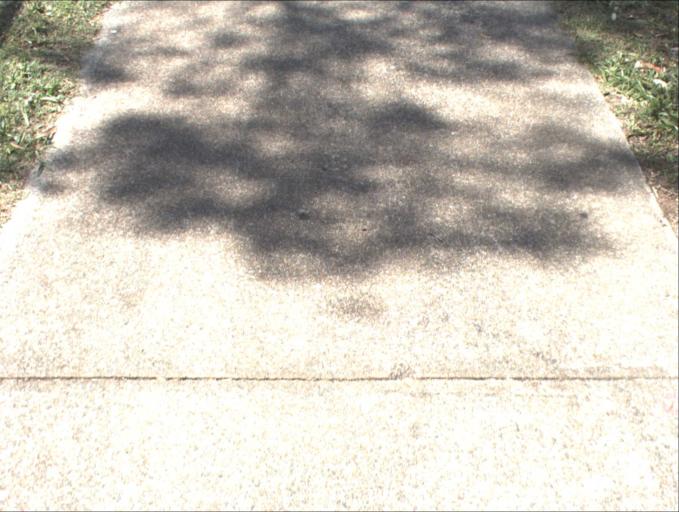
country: AU
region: Queensland
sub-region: Logan
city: Beenleigh
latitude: -27.6918
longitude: 153.2150
